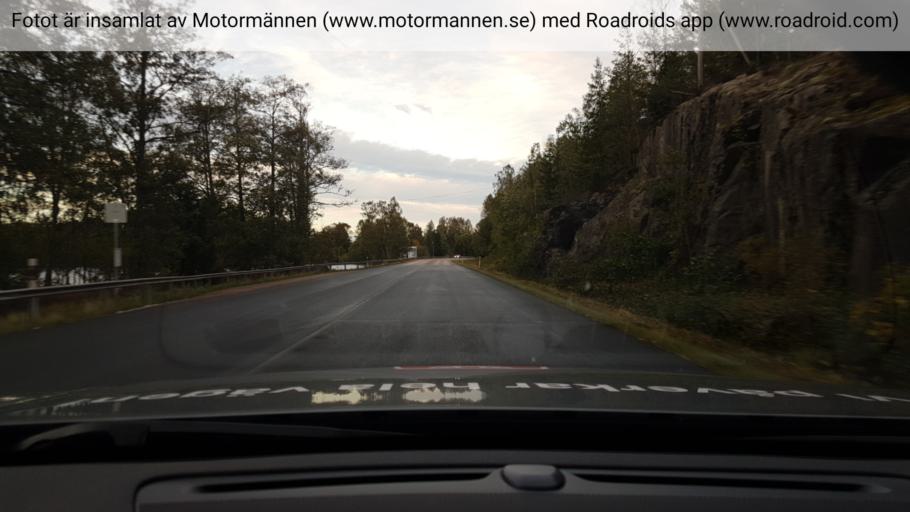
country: SE
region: Vaestra Goetaland
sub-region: Amals Kommun
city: Amal
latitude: 59.0782
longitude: 12.6029
